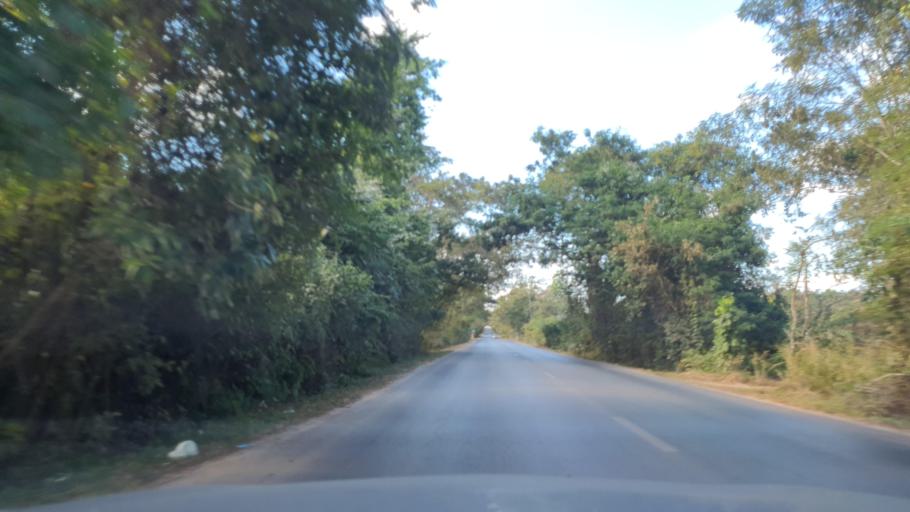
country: TH
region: Nakhon Phanom
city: Ban Phaeng
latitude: 18.0184
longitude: 104.1526
